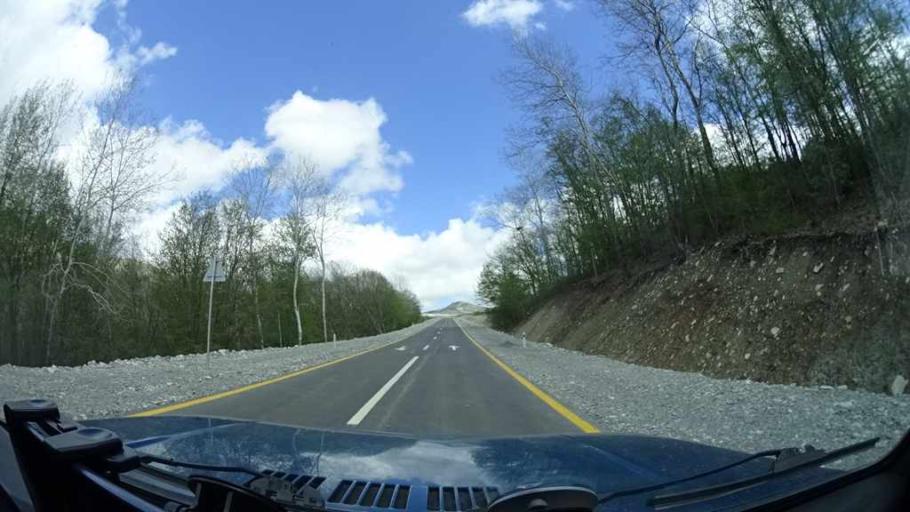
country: AZ
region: Ismayilli
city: Basqal
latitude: 40.8797
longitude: 48.4323
